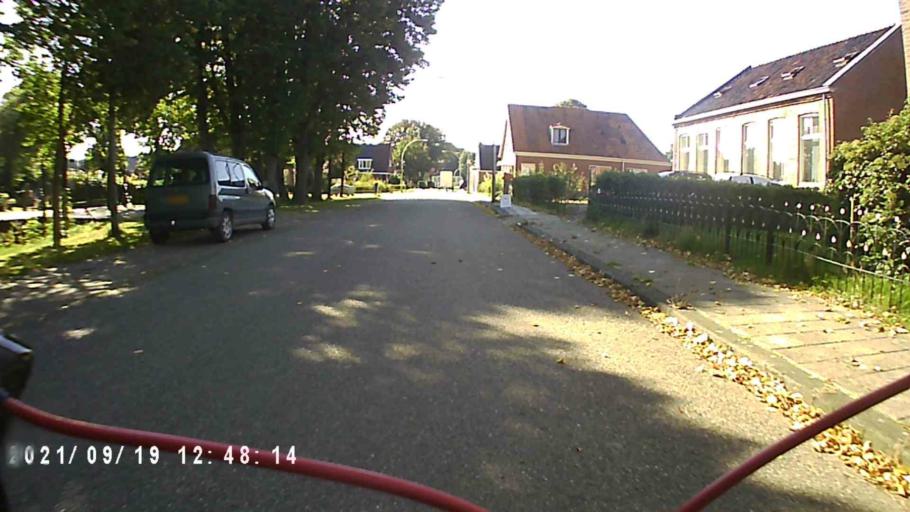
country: NL
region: Groningen
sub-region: Gemeente  Oldambt
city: Winschoten
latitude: 53.2104
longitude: 6.9419
